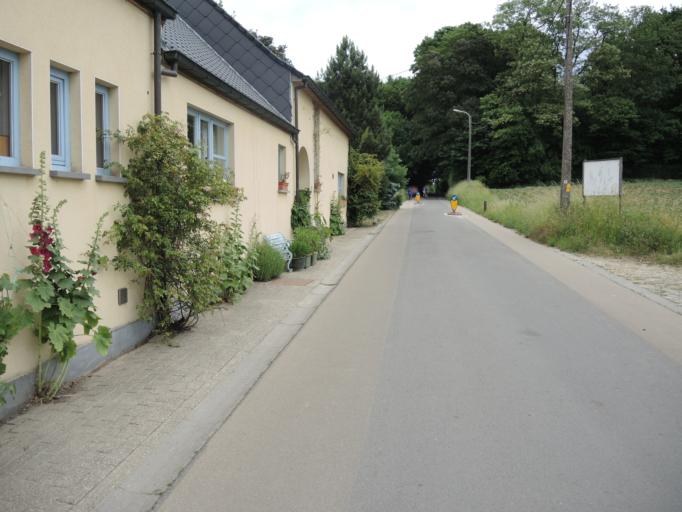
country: BE
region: Flanders
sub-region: Provincie Vlaams-Brabant
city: Asse
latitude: 50.9109
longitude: 4.1771
